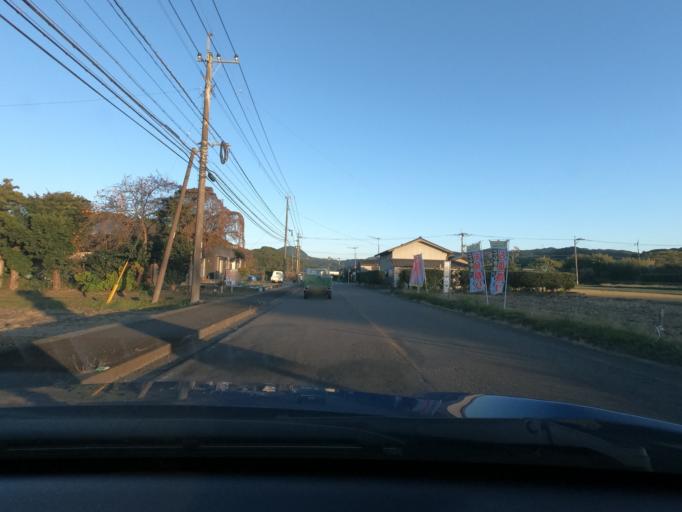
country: JP
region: Kagoshima
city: Satsumasendai
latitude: 31.7945
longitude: 130.4465
